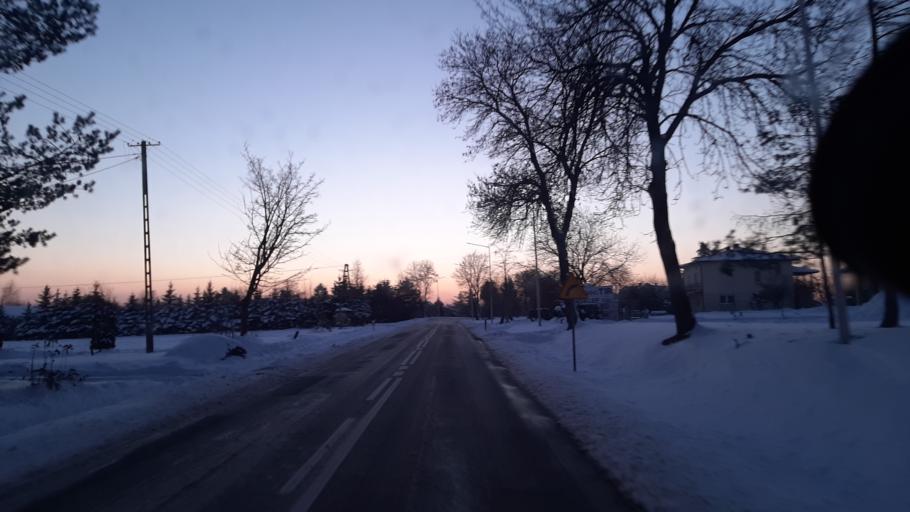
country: PL
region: Lublin Voivodeship
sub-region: Powiat lubelski
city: Jastkow
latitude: 51.3614
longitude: 22.5247
